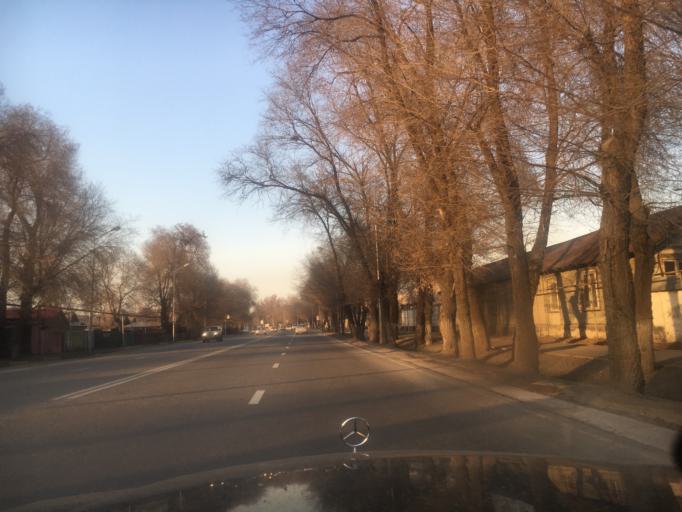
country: KZ
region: Almaty Oblysy
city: Pervomayskiy
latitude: 43.3589
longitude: 76.9799
